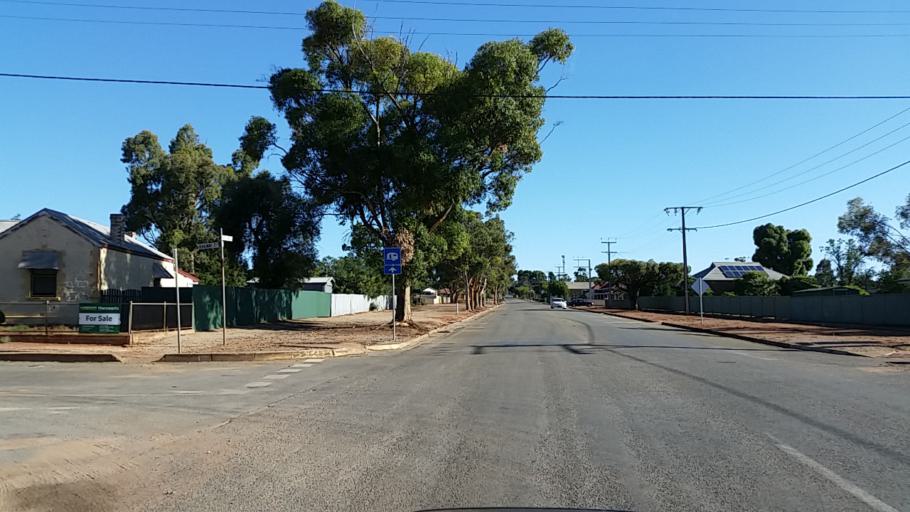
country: AU
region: South Australia
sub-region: Peterborough
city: Peterborough
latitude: -32.9750
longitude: 138.8319
